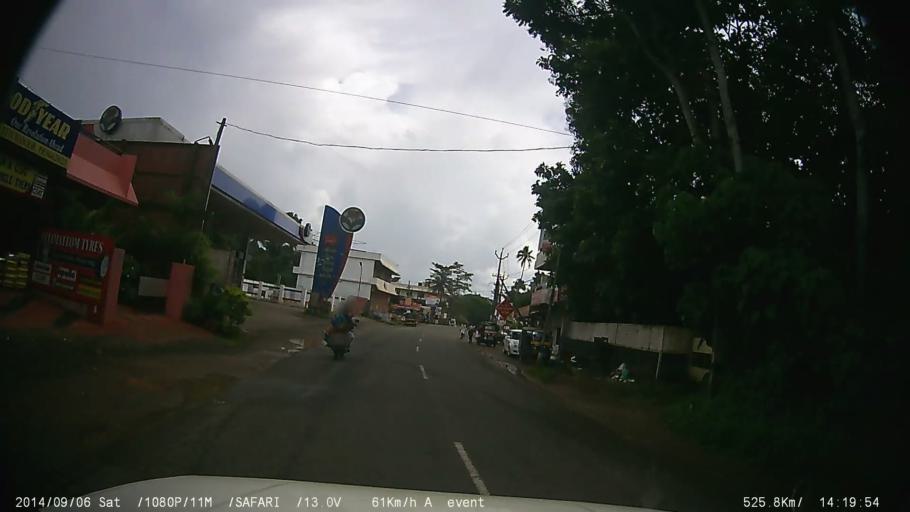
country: IN
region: Kerala
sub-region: Kottayam
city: Kottayam
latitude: 9.6561
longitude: 76.5512
